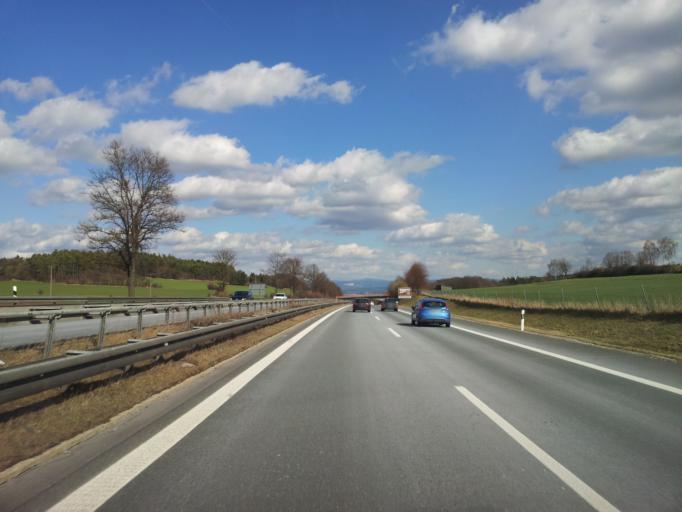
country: DE
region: Bavaria
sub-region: Upper Franconia
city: Kasendorf
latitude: 50.0094
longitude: 11.3513
